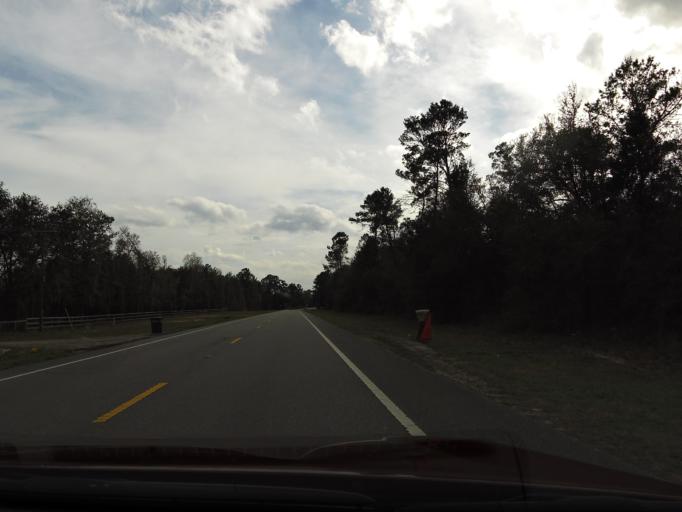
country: US
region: Florida
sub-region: Volusia County
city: De Leon Springs
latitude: 29.2102
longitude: -81.3147
